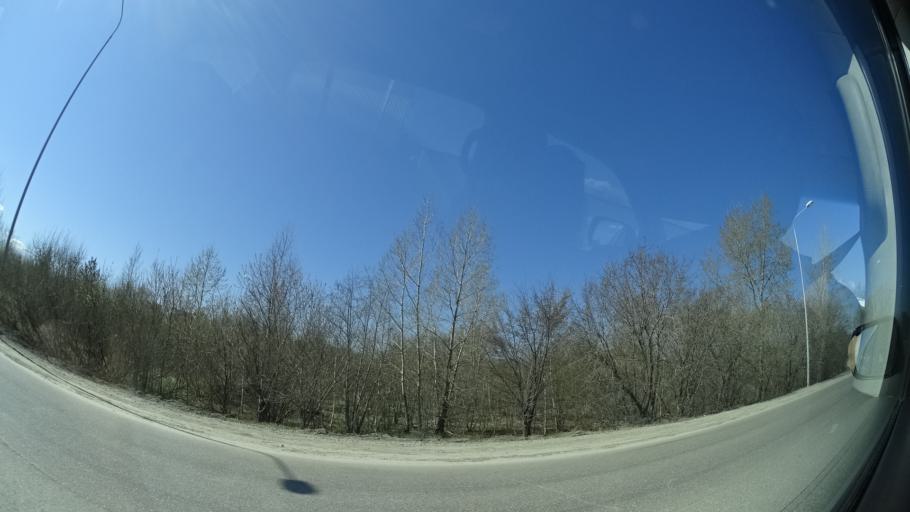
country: RU
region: Perm
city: Perm
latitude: 58.1021
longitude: 56.3212
